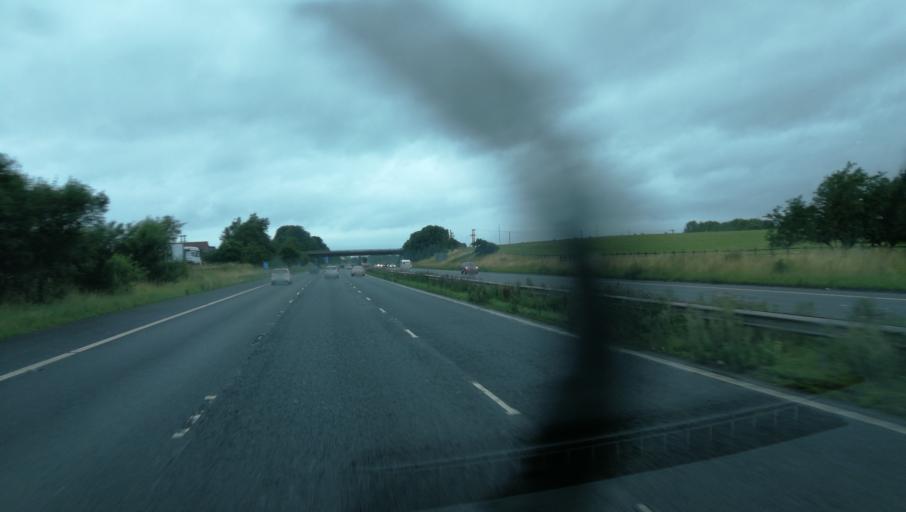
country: GB
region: England
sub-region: Borough of Bolton
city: Westhoughton
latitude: 53.5679
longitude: -2.5316
